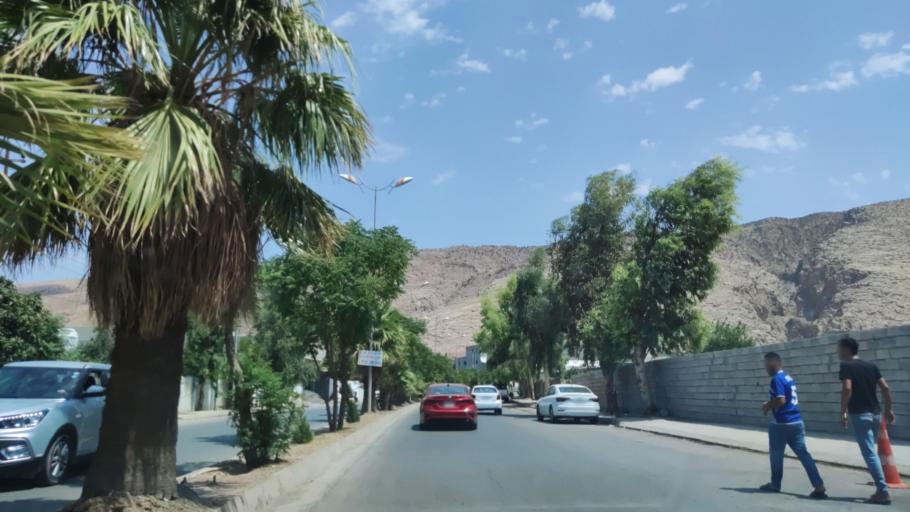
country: IQ
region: Arbil
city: Shaqlawah
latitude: 36.5472
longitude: 44.3495
